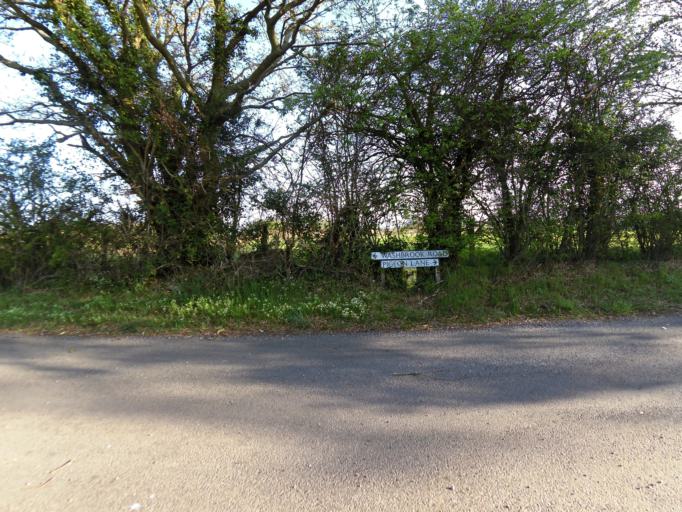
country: GB
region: England
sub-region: Suffolk
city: Bramford
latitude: 52.0447
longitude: 1.0716
